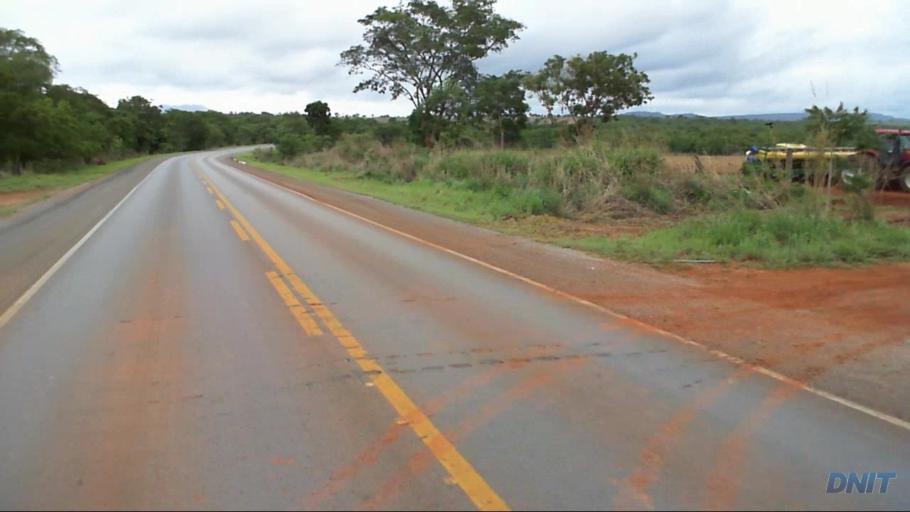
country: BR
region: Goias
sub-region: Padre Bernardo
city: Padre Bernardo
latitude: -15.2208
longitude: -48.5455
